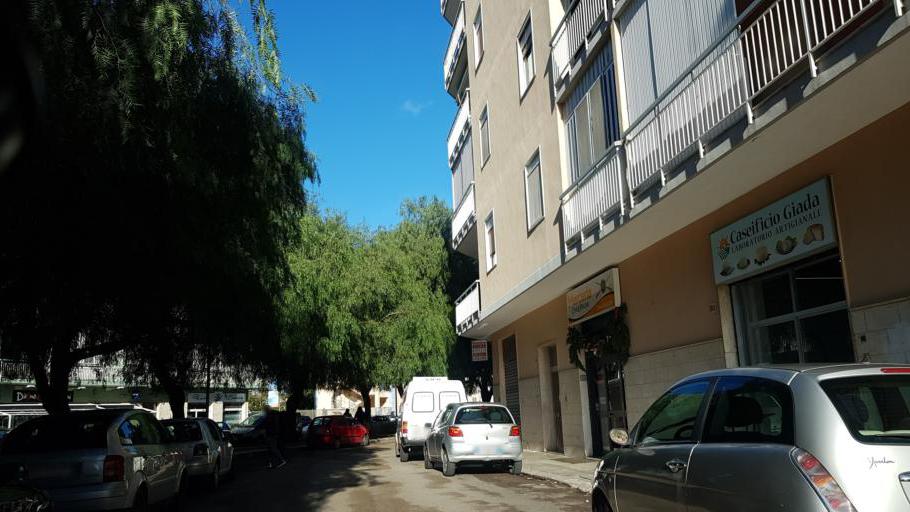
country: IT
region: Apulia
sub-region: Provincia di Brindisi
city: Brindisi
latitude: 40.6248
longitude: 17.9247
